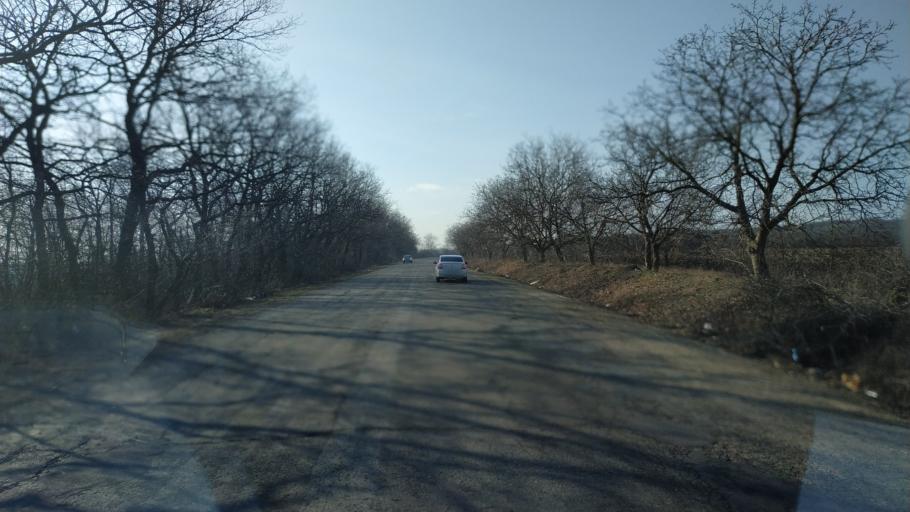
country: MD
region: Chisinau
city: Singera
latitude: 46.8703
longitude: 29.0398
